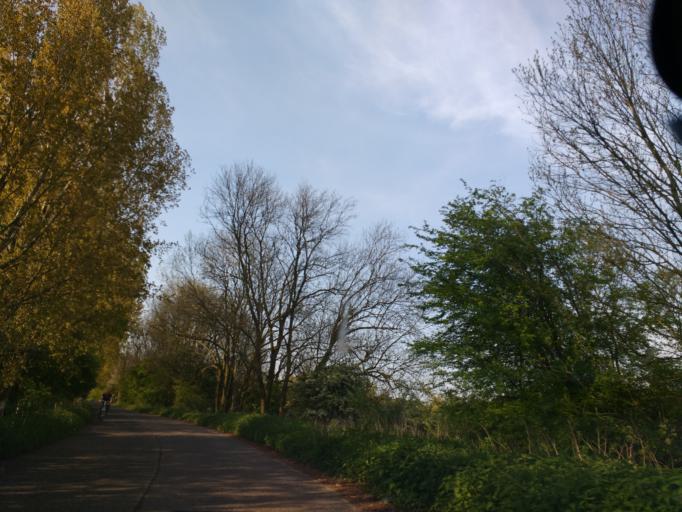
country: NL
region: Gelderland
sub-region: Gemeente Wageningen
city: Wageningen
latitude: 51.9438
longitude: 5.6206
